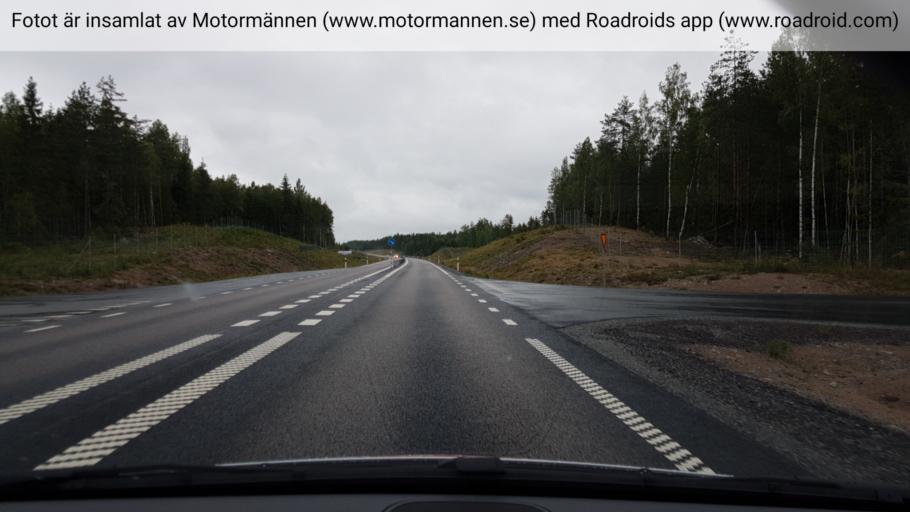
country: SE
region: Uppsala
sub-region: Heby Kommun
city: Tarnsjo
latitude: 60.0803
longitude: 16.9149
